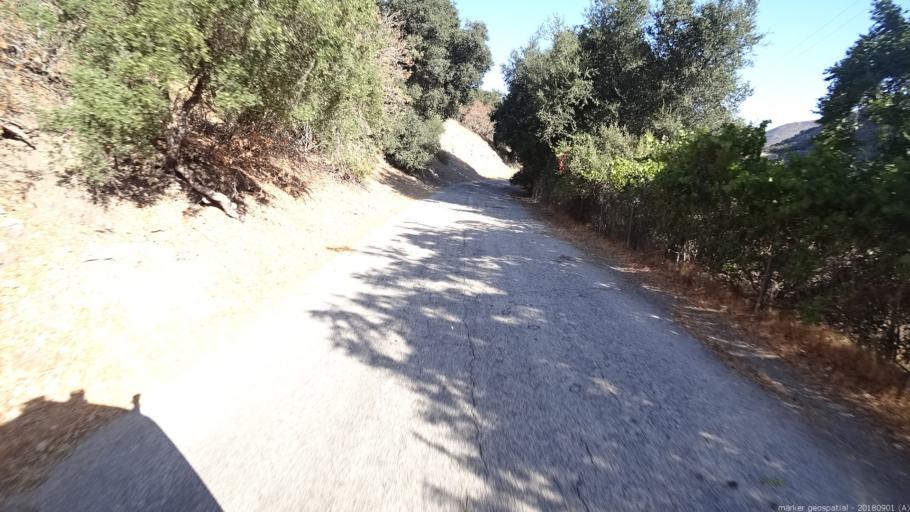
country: US
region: California
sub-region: Monterey County
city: Greenfield
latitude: 36.2102
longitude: -121.2797
